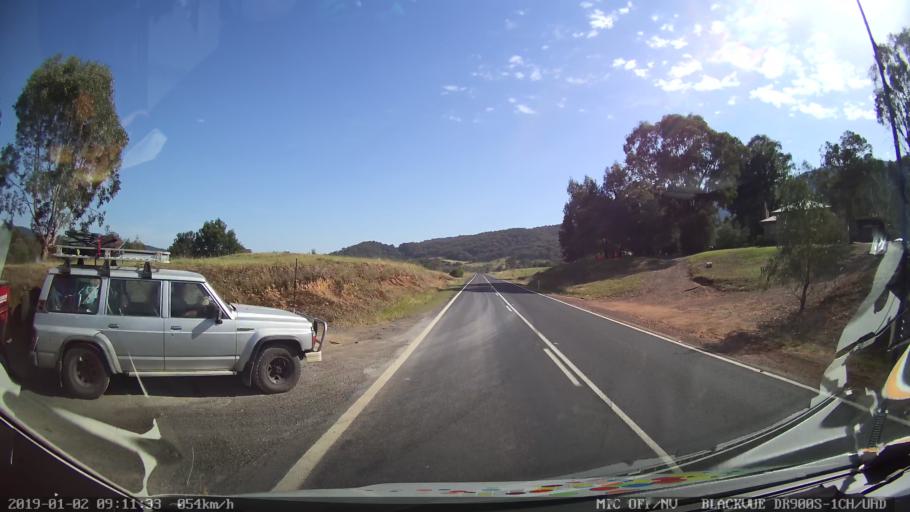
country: AU
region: New South Wales
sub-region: Tumut Shire
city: Tumut
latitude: -35.5104
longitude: 148.2692
